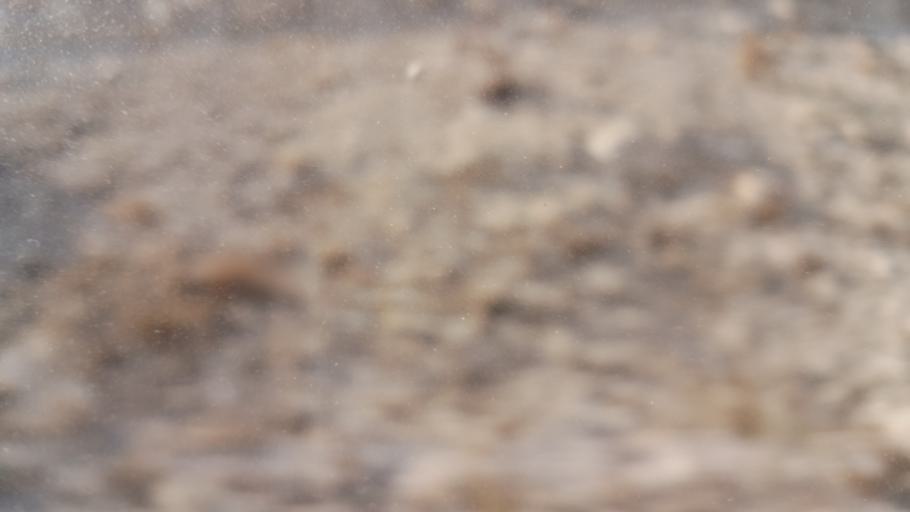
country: TR
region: Eskisehir
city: Kirka
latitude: 39.3477
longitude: 30.5871
